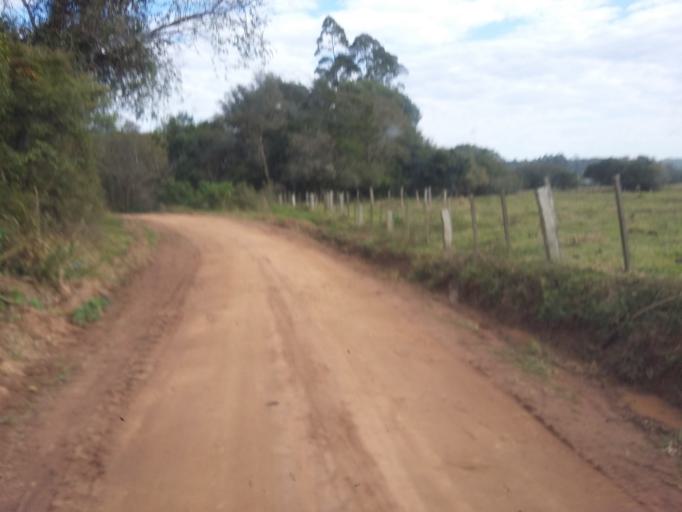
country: BR
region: Rio Grande do Sul
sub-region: Camaqua
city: Camaqua
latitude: -30.7127
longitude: -51.7818
